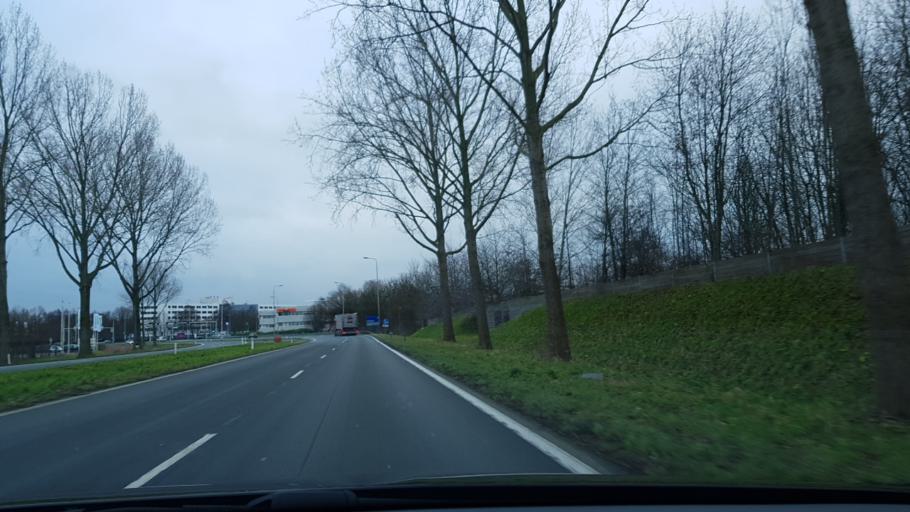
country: NL
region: North Holland
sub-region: Gemeente Haarlemmermeer
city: Hoofddorp
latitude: 52.2997
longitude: 4.7104
